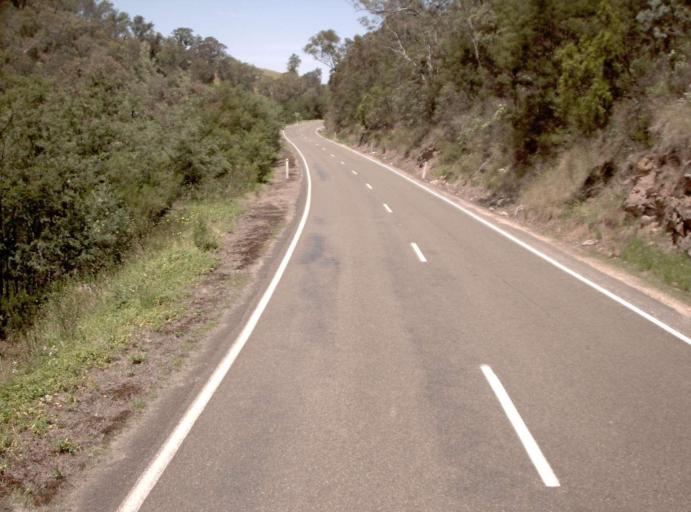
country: AU
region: Victoria
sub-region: East Gippsland
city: Bairnsdale
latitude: -37.4885
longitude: 147.8331
